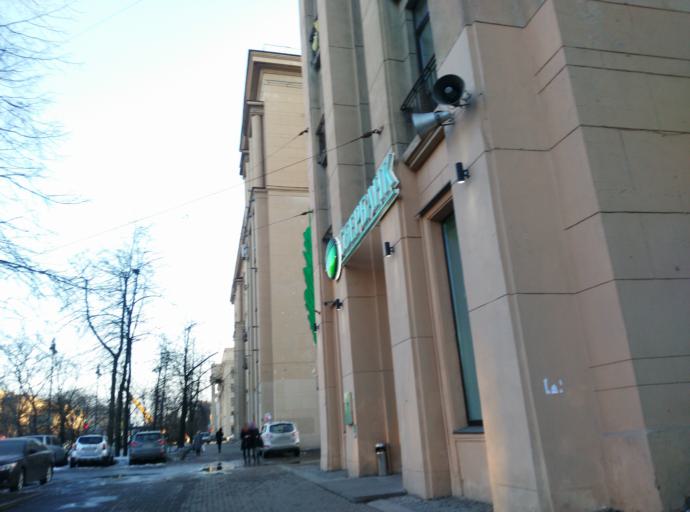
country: RU
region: St.-Petersburg
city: Kupchino
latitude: 59.8771
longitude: 30.3194
